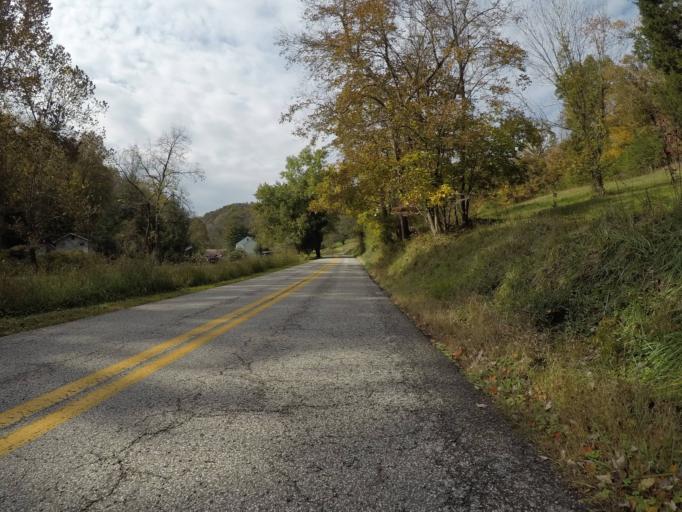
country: US
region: West Virginia
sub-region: Cabell County
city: Huntington
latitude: 38.3781
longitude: -82.4014
